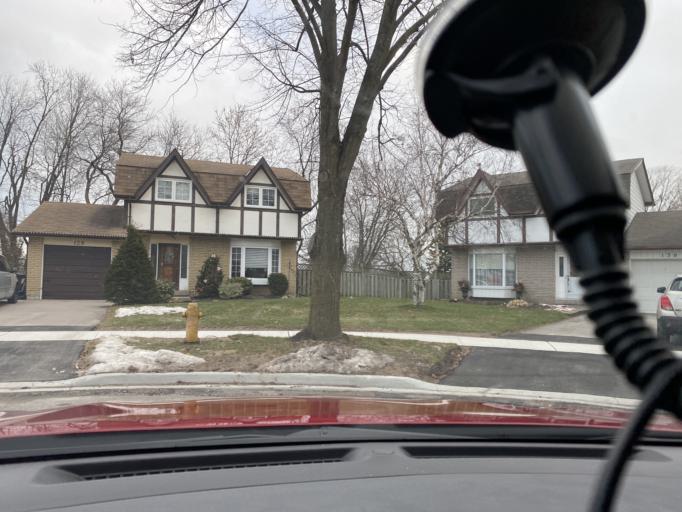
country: CA
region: Ontario
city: Pickering
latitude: 43.7959
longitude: -79.1360
